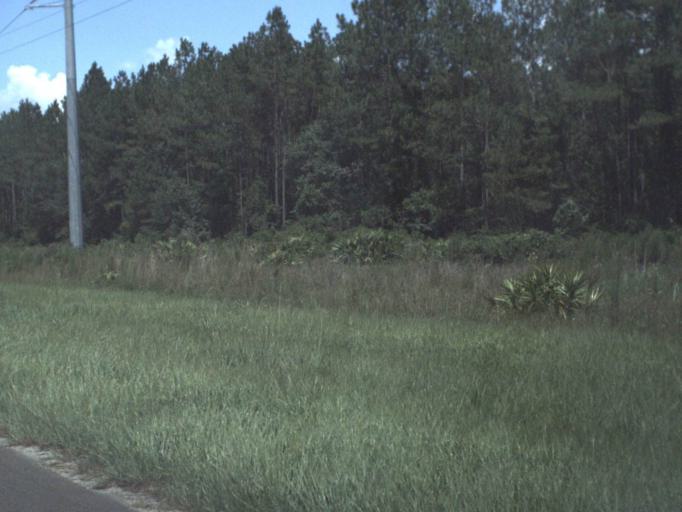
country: US
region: Florida
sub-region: Gilchrist County
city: Trenton
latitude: 29.6535
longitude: -82.7856
